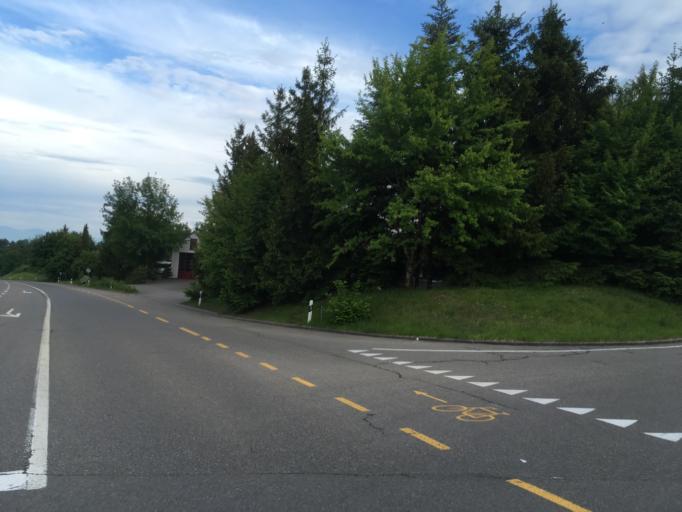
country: CH
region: Zurich
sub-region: Bezirk Uster
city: Pfaffhausen
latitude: 47.3607
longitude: 8.6238
